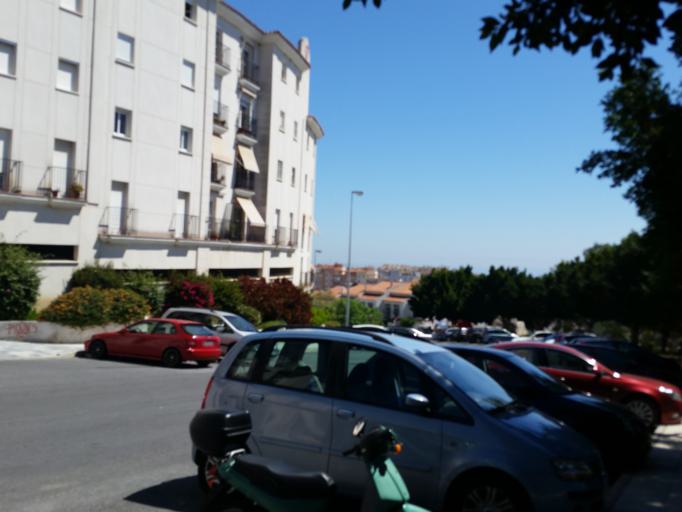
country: ES
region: Andalusia
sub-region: Provincia de Malaga
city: Benalmadena
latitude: 36.6031
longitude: -4.5385
